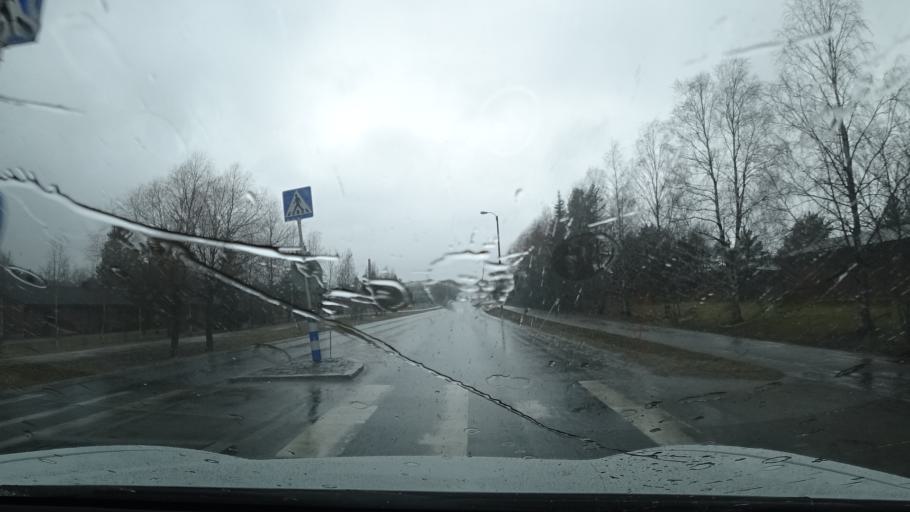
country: FI
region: Paijanne Tavastia
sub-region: Lahti
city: Orimattila
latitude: 60.8022
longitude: 25.7424
